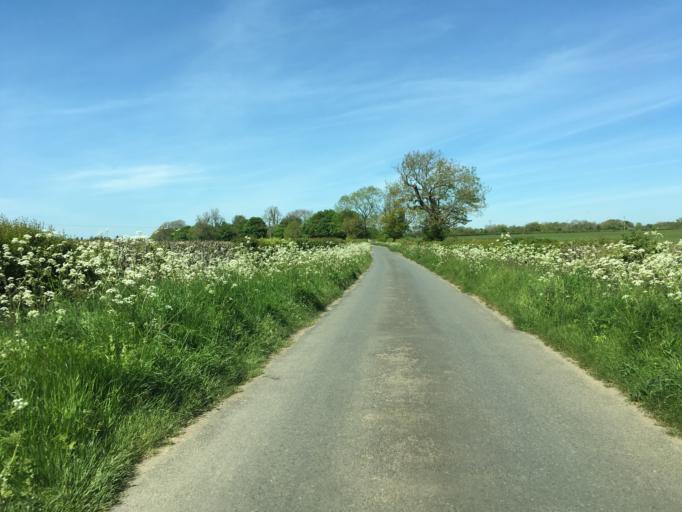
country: GB
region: England
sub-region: Gloucestershire
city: Cirencester
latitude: 51.6786
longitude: -1.9949
